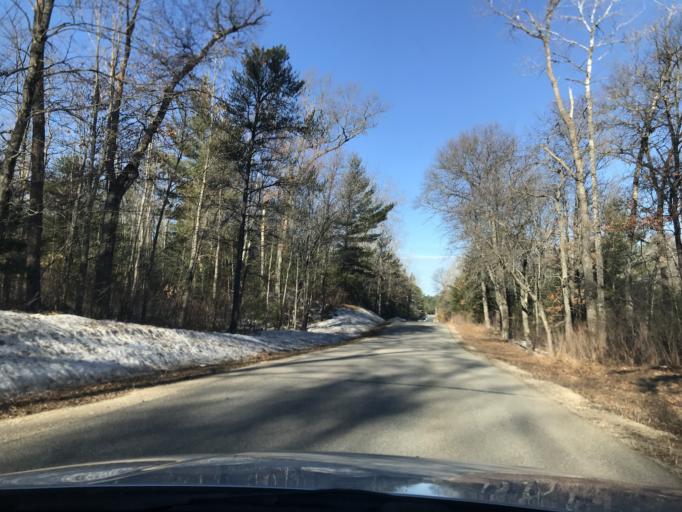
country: US
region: Wisconsin
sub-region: Marinette County
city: Niagara
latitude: 45.3981
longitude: -88.0834
